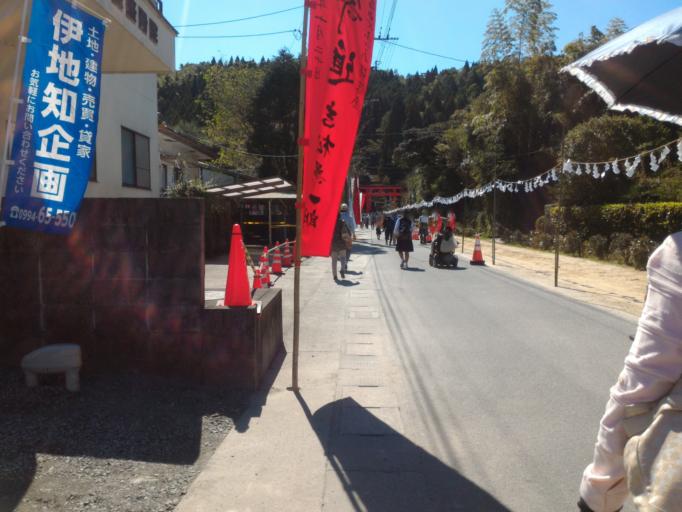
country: JP
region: Kagoshima
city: Kanoya
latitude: 31.3446
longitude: 130.9471
